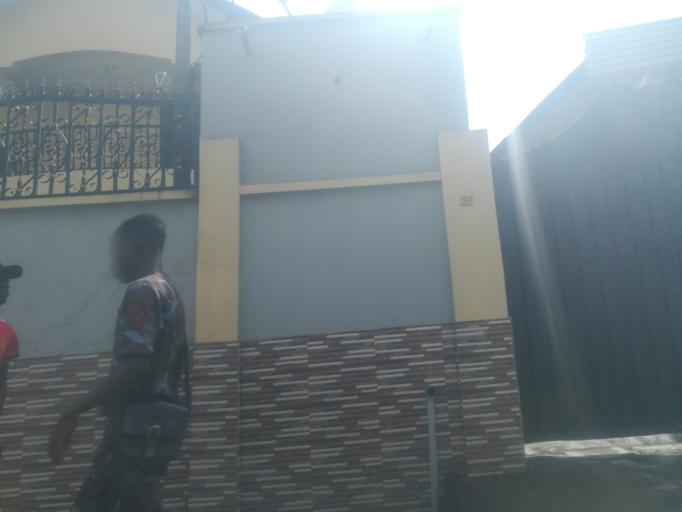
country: NG
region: Lagos
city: Somolu
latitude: 6.5478
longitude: 3.3723
